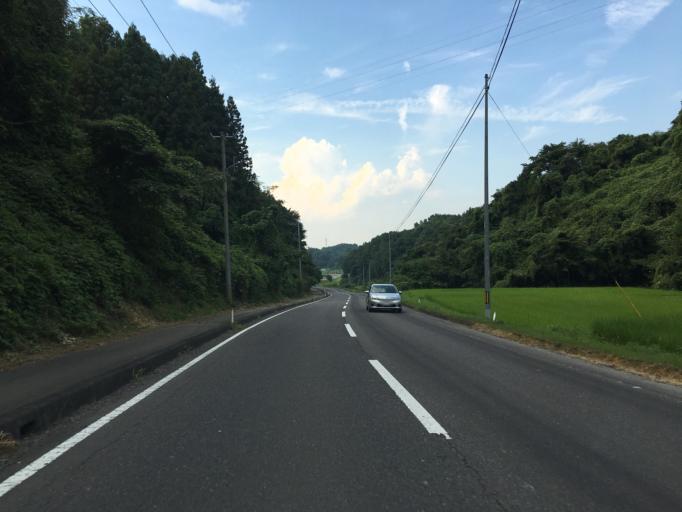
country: JP
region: Fukushima
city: Nihommatsu
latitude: 37.5401
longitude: 140.4417
